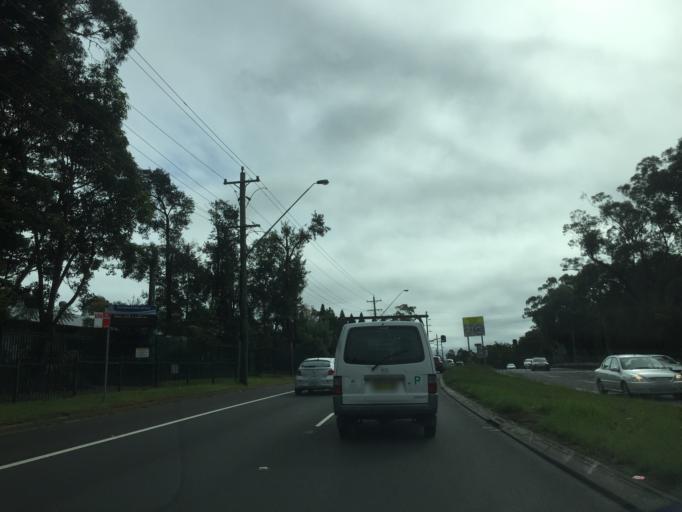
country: AU
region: New South Wales
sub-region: Blue Mountains Municipality
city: Blaxland
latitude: -33.7375
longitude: 150.6049
